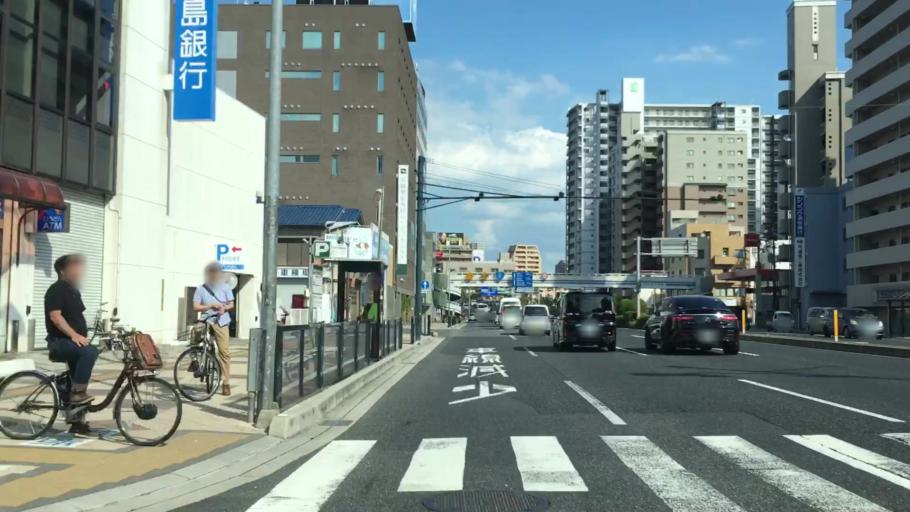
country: JP
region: Hiroshima
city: Hiroshima-shi
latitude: 34.3863
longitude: 132.4434
